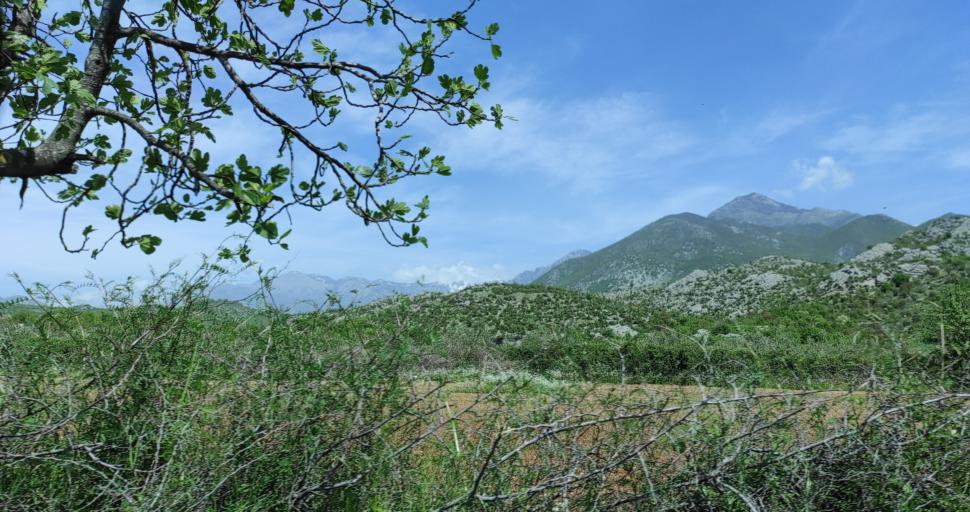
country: AL
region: Shkoder
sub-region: Rrethi i Malesia e Madhe
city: Gruemire
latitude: 42.1498
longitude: 19.5362
